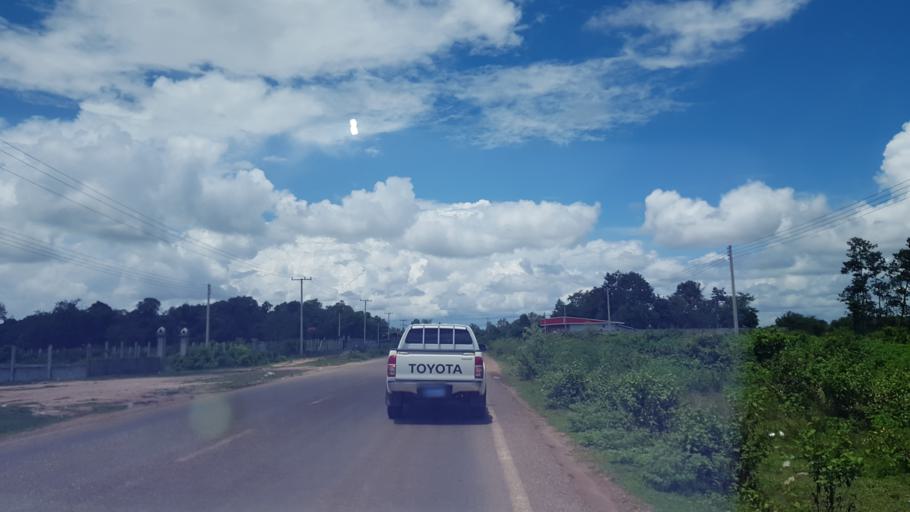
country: LA
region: Vientiane
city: Vientiane
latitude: 18.1145
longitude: 102.5866
